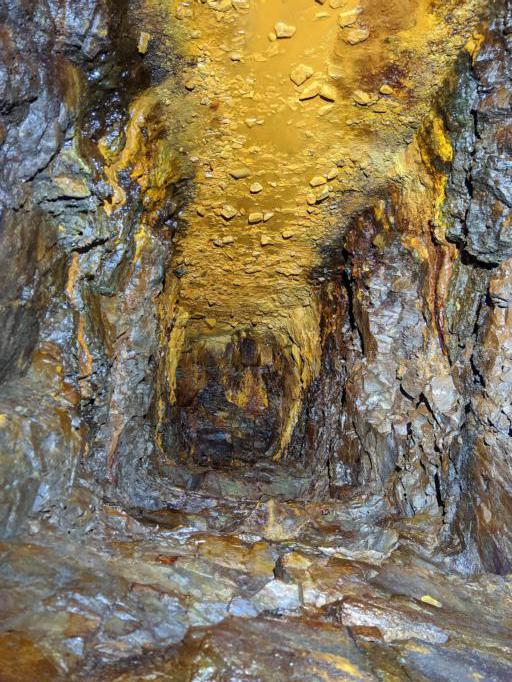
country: NO
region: Akershus
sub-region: Eidsvoll
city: Eidsvoll
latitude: 60.4221
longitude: 11.1943
